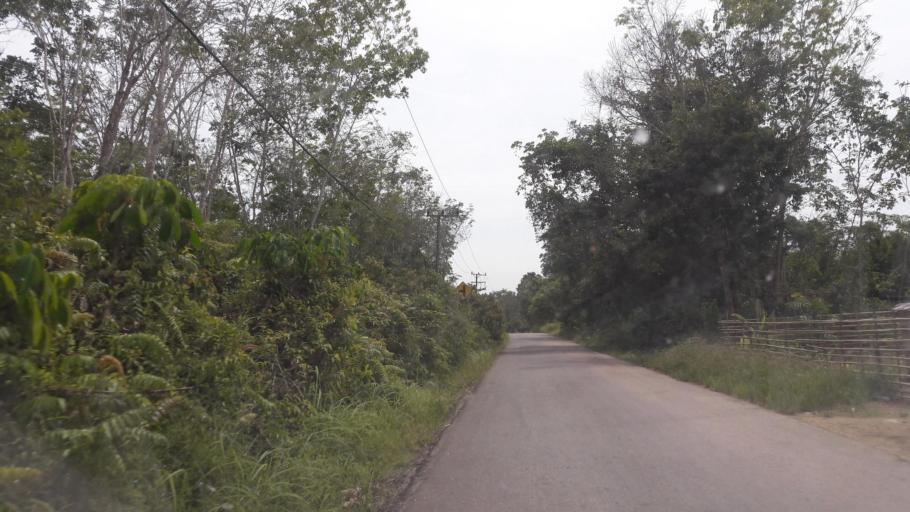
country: ID
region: South Sumatra
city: Gunungmenang
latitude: -3.1355
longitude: 104.1120
